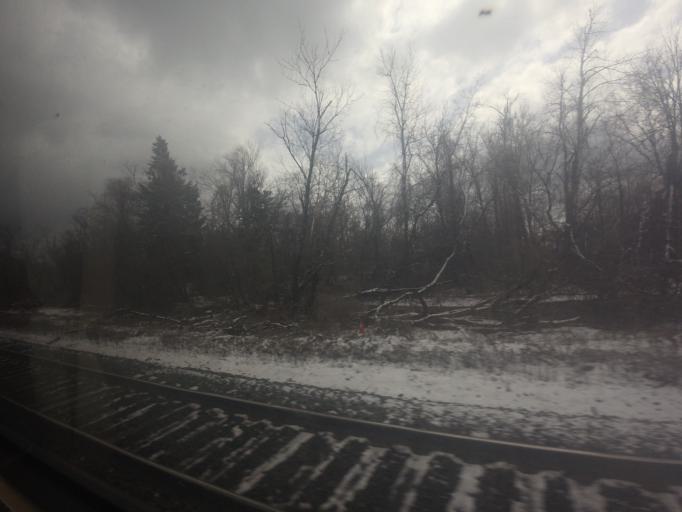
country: CA
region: Ontario
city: Scarborough
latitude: 43.7586
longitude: -79.1788
